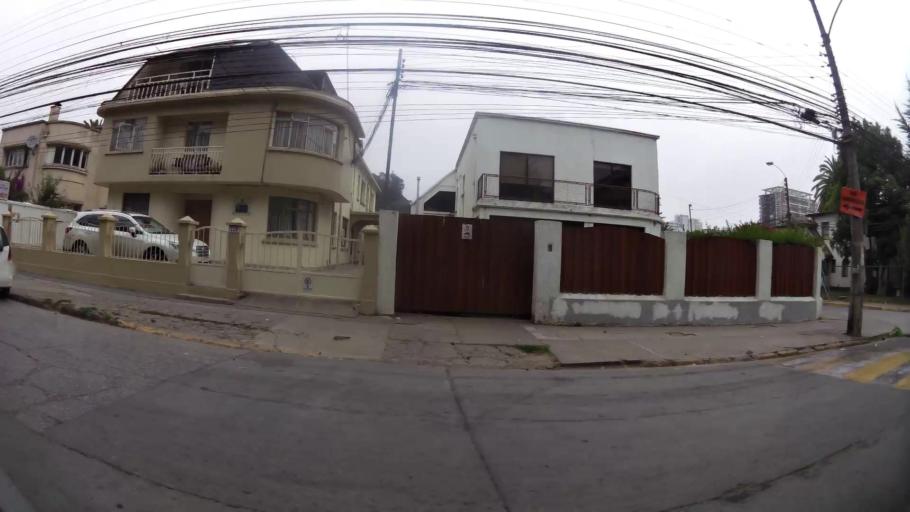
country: CL
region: Biobio
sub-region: Provincia de Concepcion
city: Concepcion
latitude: -36.8294
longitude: -73.0384
